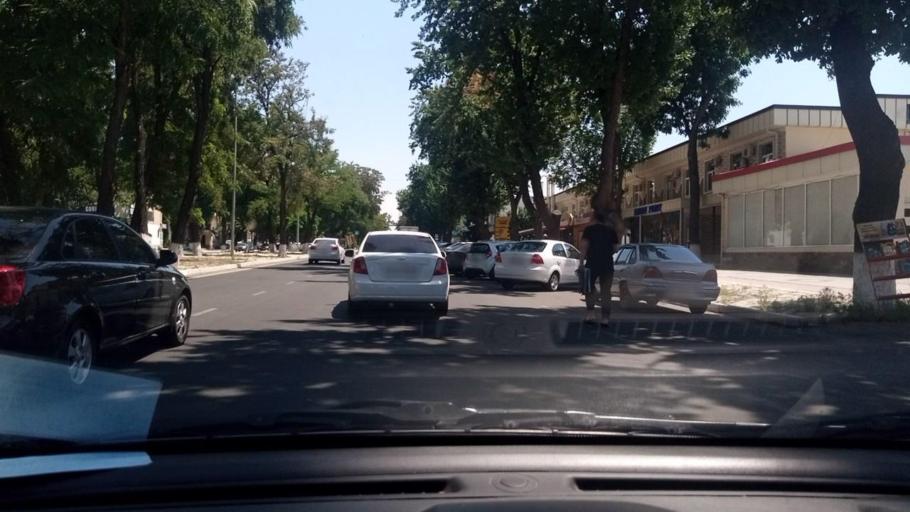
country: UZ
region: Toshkent Shahri
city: Tashkent
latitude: 41.2933
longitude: 69.1982
